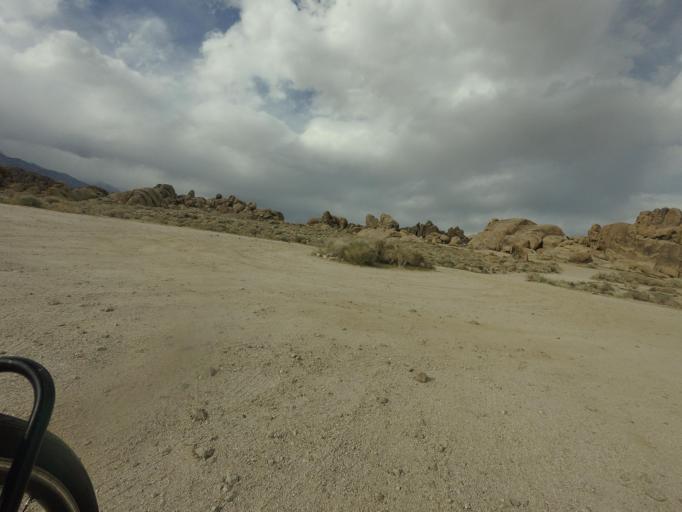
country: US
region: California
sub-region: Inyo County
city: Lone Pine
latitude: 36.5990
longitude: -118.1165
